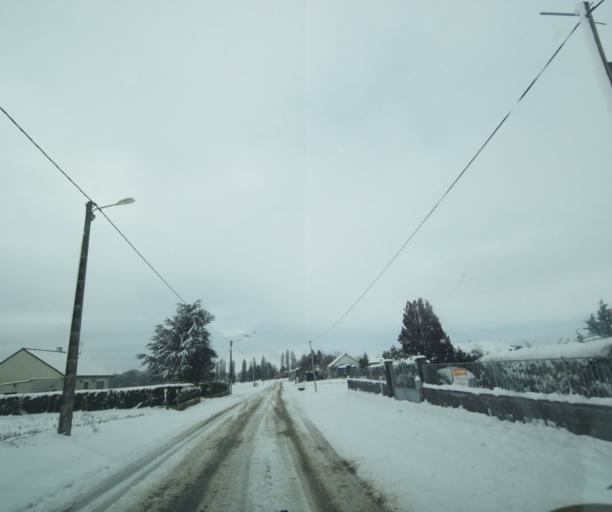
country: FR
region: Champagne-Ardenne
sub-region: Departement de la Haute-Marne
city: Montier-en-Der
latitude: 48.5249
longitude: 4.7167
